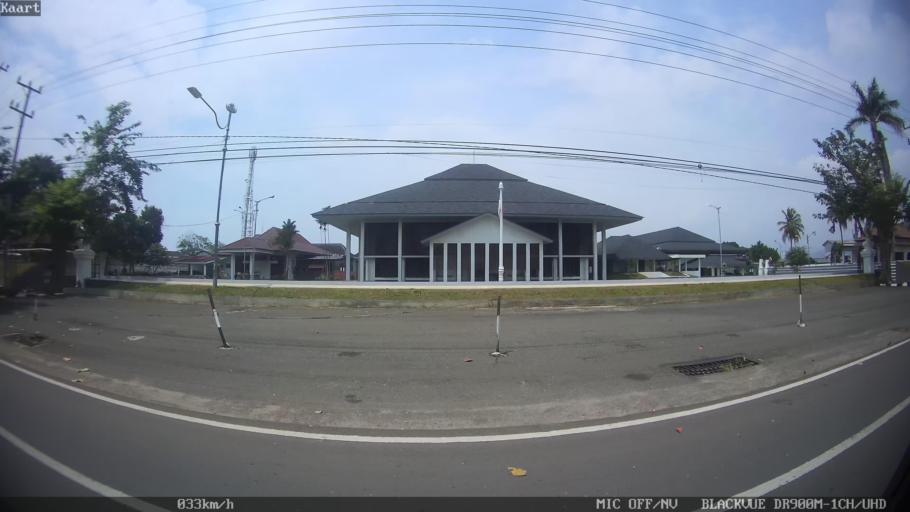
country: ID
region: Lampung
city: Bandarlampung
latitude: -5.4295
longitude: 105.2656
